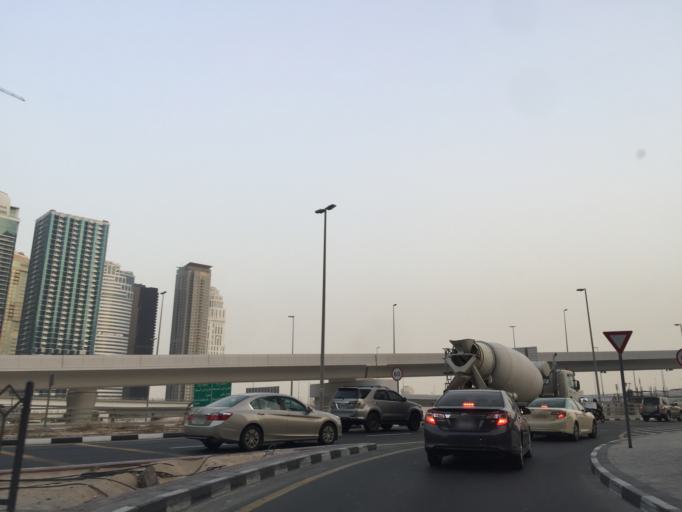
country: AE
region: Dubai
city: Dubai
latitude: 25.0693
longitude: 55.1352
